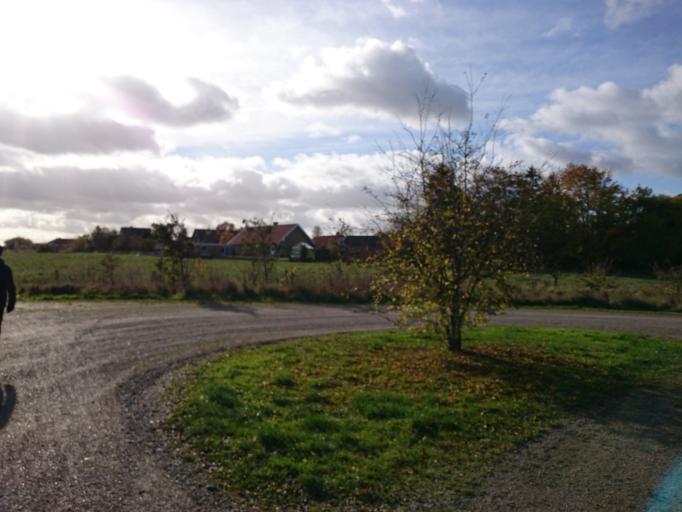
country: DK
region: South Denmark
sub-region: Odense Kommune
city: Hojby
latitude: 55.3289
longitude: 10.4316
